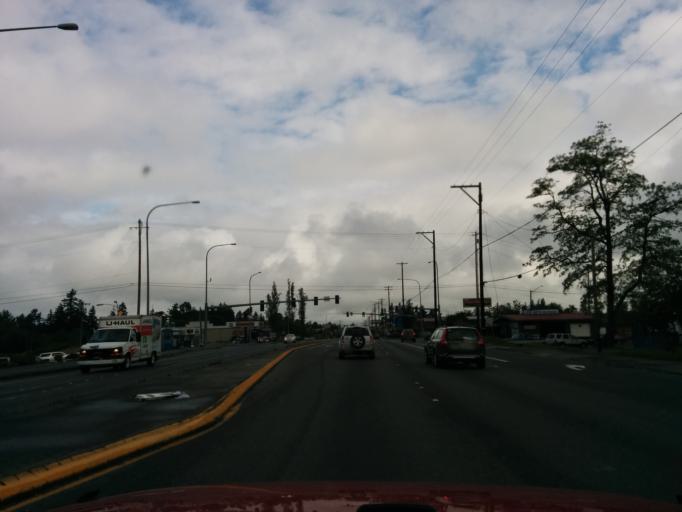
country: US
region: Washington
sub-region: Snohomish County
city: Martha Lake
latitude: 47.8816
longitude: -122.2792
